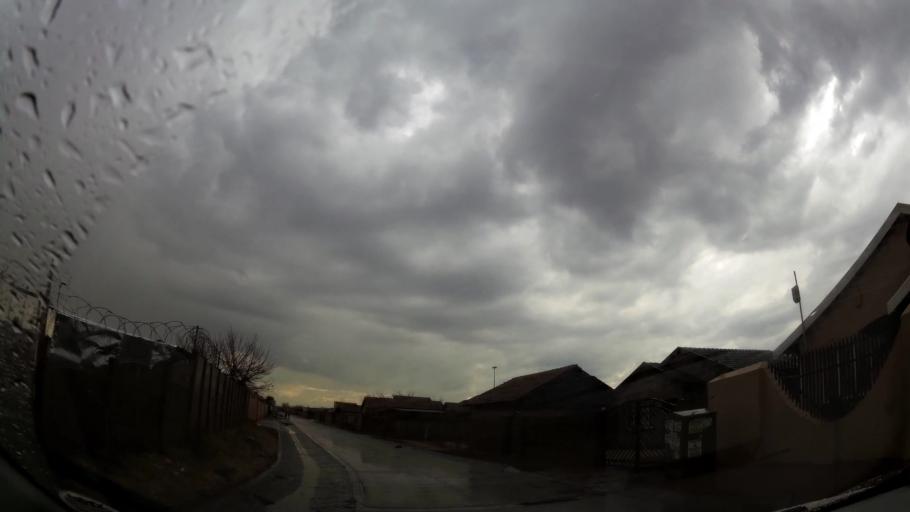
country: ZA
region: Gauteng
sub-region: Ekurhuleni Metropolitan Municipality
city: Germiston
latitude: -26.3652
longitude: 28.1353
